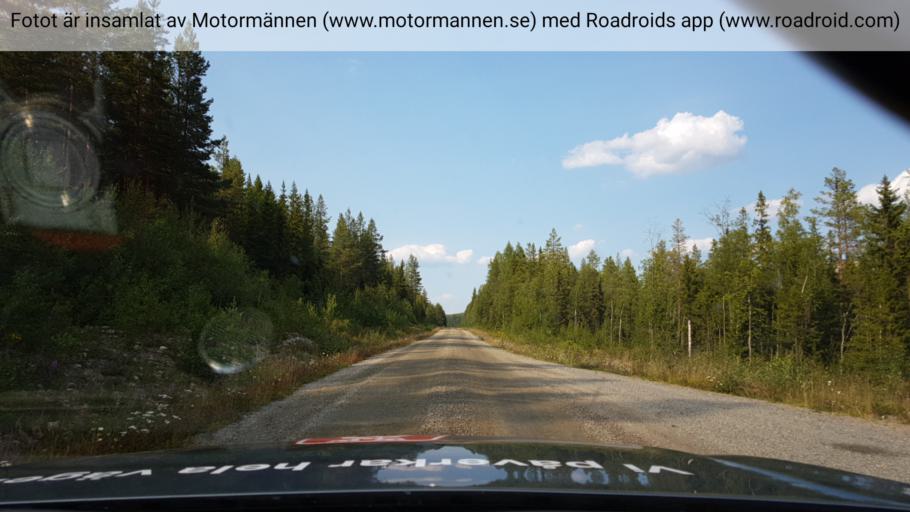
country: SE
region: Jaemtland
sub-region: Bergs Kommun
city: Hoverberg
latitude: 62.5630
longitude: 14.8984
